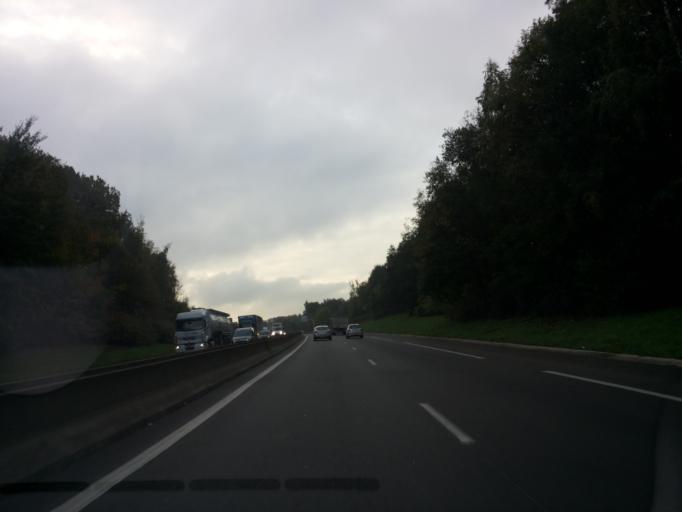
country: FR
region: Champagne-Ardenne
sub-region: Departement des Ardennes
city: La Francheville
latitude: 49.7444
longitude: 4.7056
